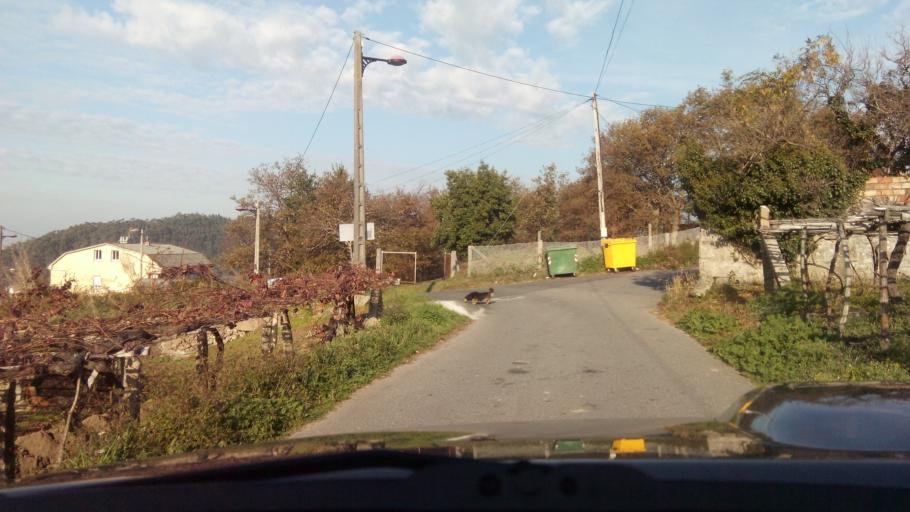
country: ES
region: Galicia
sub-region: Provincia de Pontevedra
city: Marin
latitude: 42.3571
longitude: -8.7321
